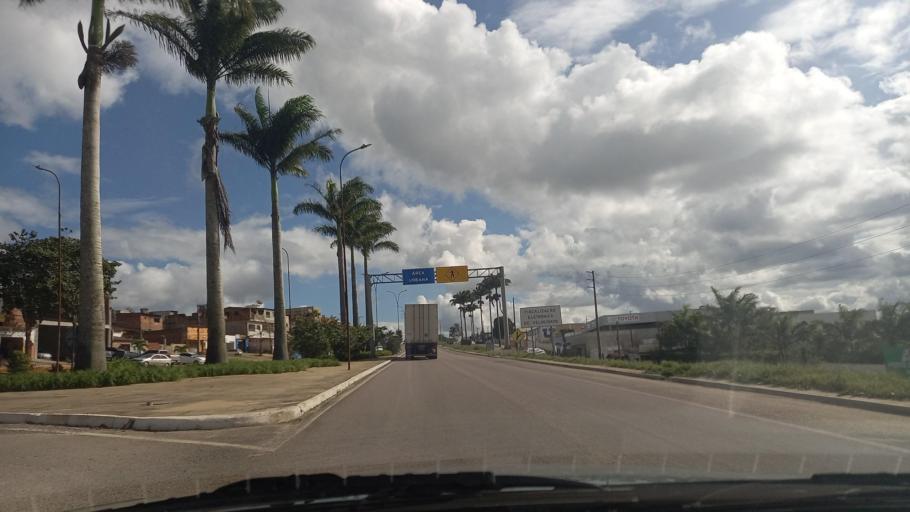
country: BR
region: Pernambuco
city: Garanhuns
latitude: -8.8742
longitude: -36.4700
